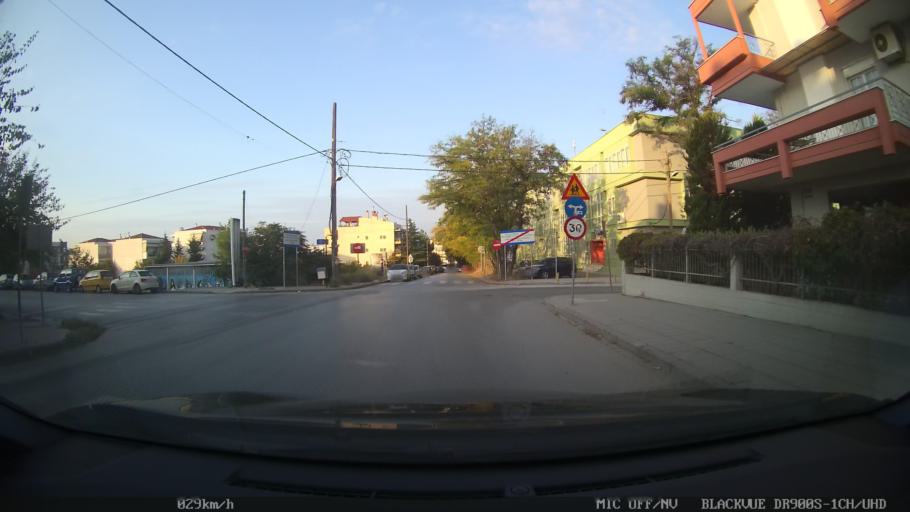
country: GR
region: Central Macedonia
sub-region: Nomos Thessalonikis
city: Pylaia
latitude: 40.5954
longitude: 22.9756
